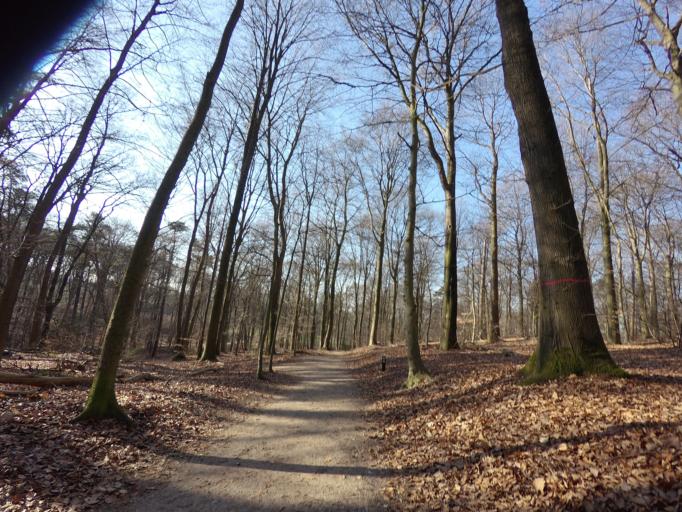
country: NL
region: Gelderland
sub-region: Gemeente Lochem
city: Barchem
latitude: 52.1411
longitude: 6.4272
